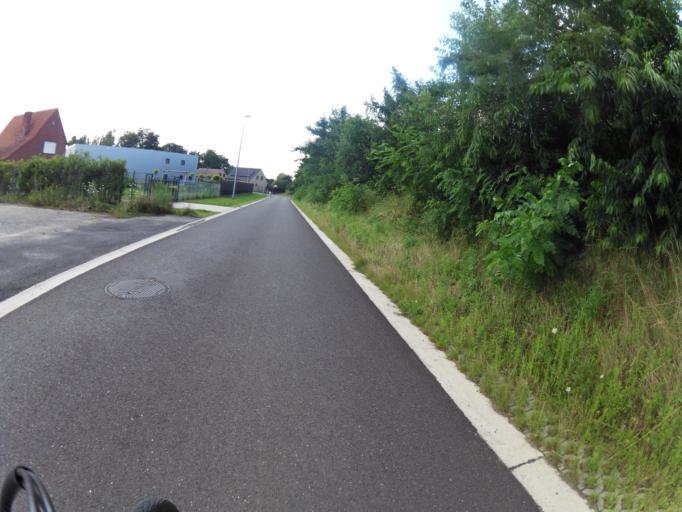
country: BE
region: Flanders
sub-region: Provincie Antwerpen
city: Balen
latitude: 51.1762
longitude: 5.1501
